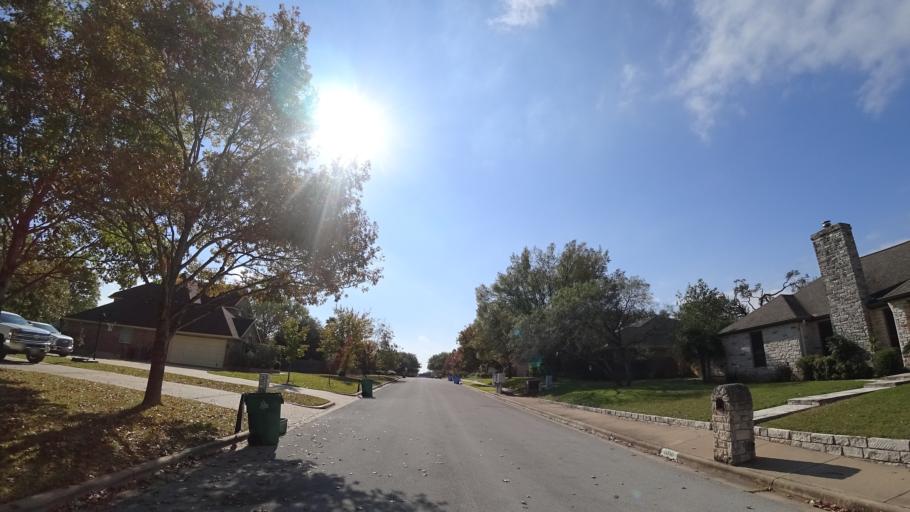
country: US
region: Texas
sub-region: Travis County
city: Shady Hollow
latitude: 30.1649
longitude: -97.8701
